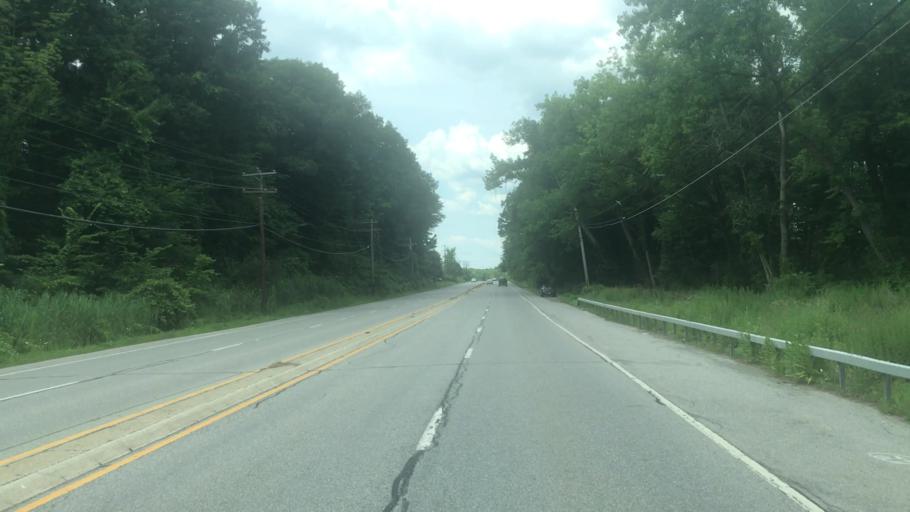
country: US
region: New York
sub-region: Putnam County
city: Peach Lake
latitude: 41.3889
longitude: -73.5892
